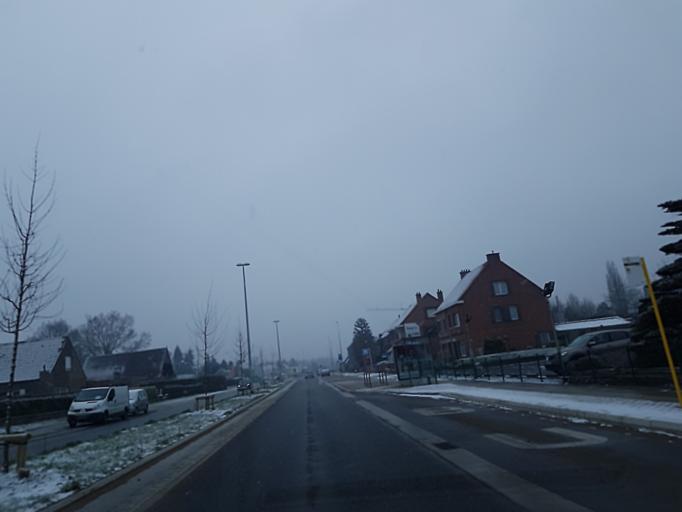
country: BE
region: Flanders
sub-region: Provincie Oost-Vlaanderen
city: Sint-Niklaas
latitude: 51.1804
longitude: 4.1950
